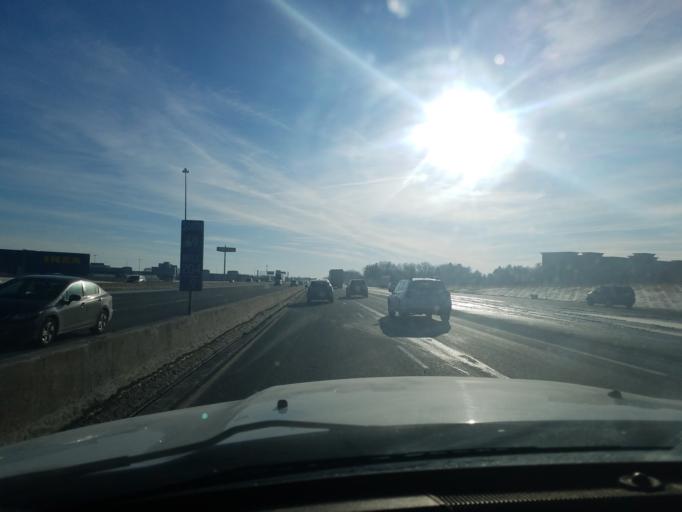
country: US
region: Indiana
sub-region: Hamilton County
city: Fishers
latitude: 39.9565
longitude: -86.0081
